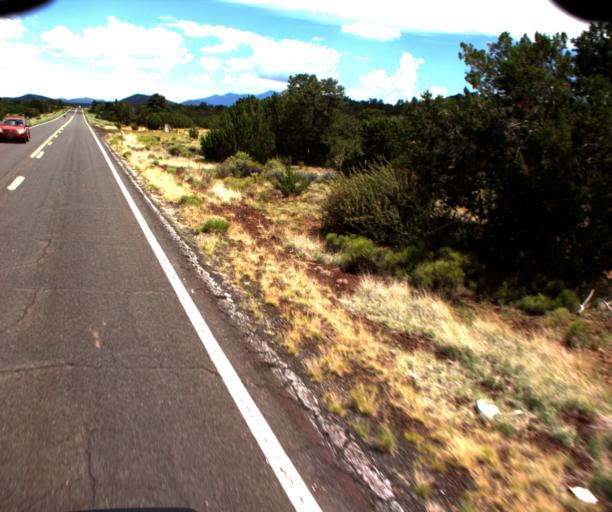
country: US
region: Arizona
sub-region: Coconino County
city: Parks
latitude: 35.5571
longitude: -111.8742
